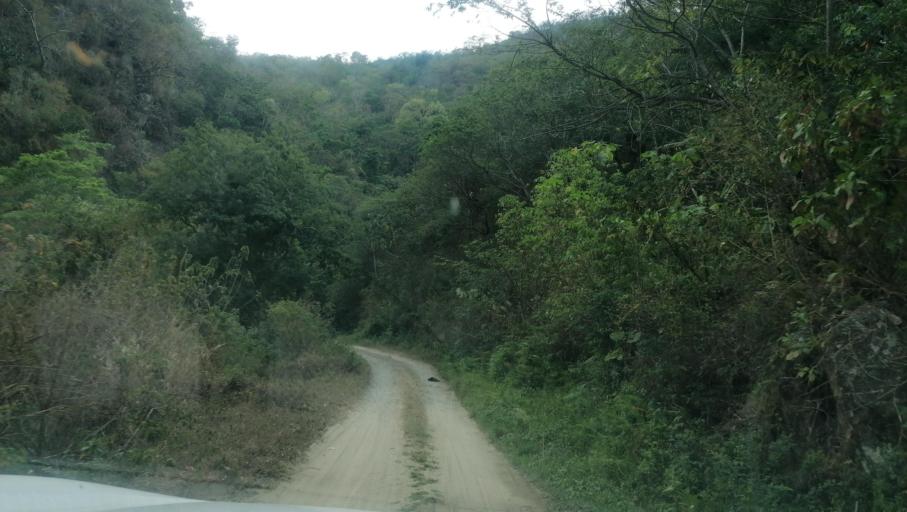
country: MX
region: Chiapas
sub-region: Cacahoatan
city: Benito Juarez
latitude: 15.1519
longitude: -92.1853
